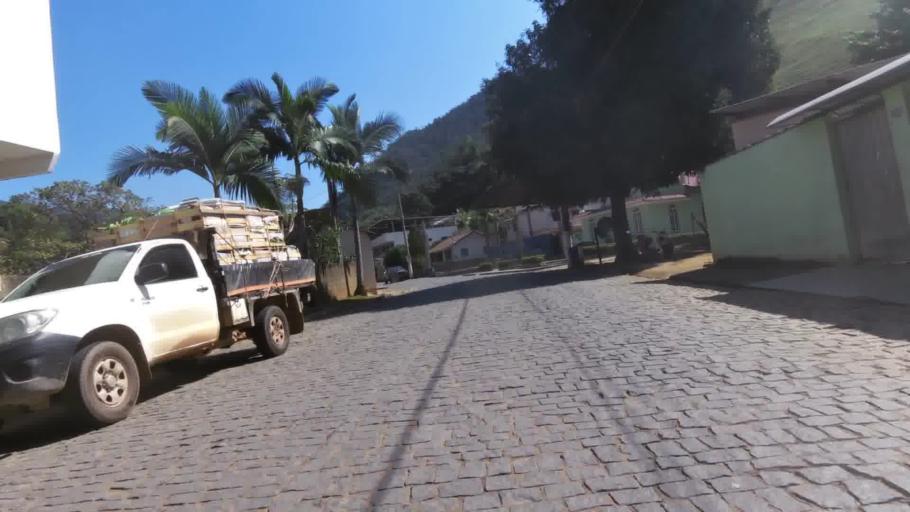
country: BR
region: Espirito Santo
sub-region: Alfredo Chaves
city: Alfredo Chaves
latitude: -20.6288
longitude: -40.7650
